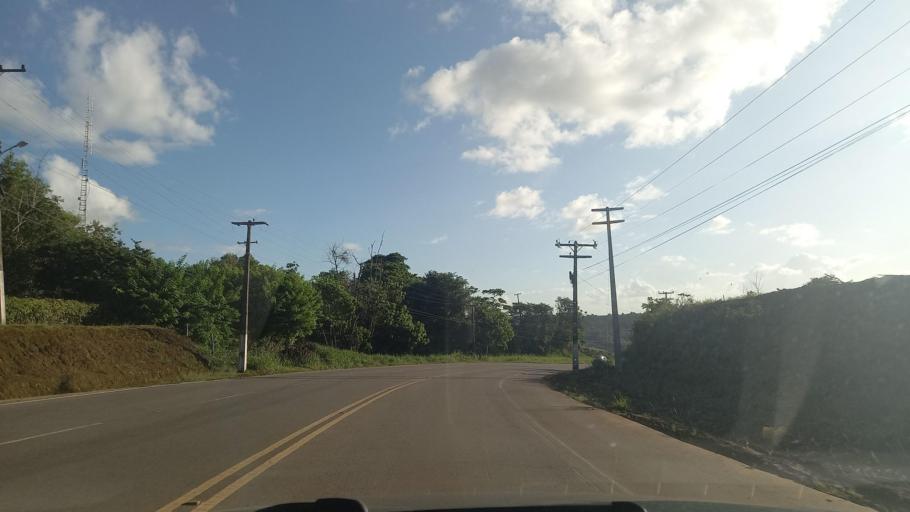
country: BR
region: Alagoas
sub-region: Sao Miguel Dos Campos
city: Sao Miguel dos Campos
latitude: -9.8088
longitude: -36.2115
